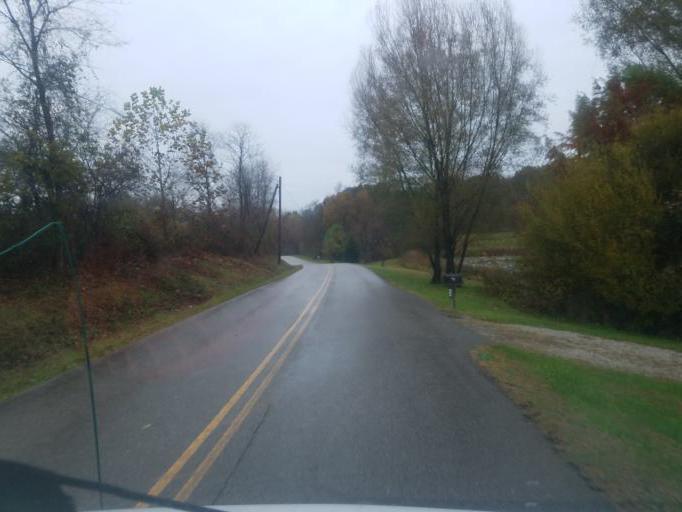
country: US
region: Ohio
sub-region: Washington County
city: Beverly
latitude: 39.4578
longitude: -81.6290
